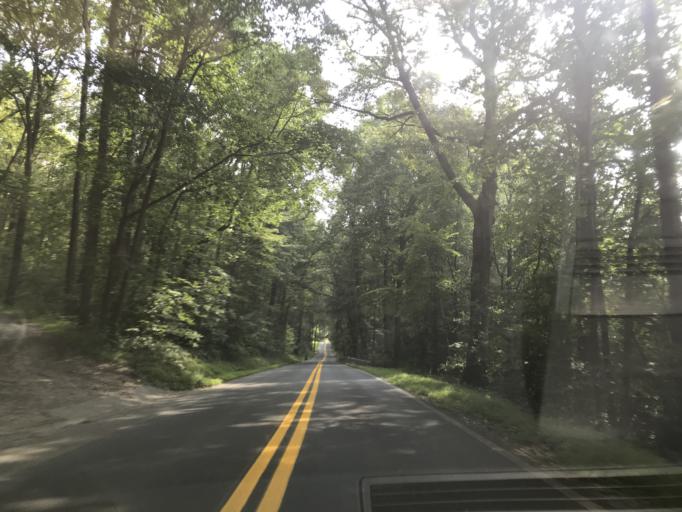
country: US
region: Maryland
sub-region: Carroll County
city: Manchester
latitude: 39.6704
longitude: -76.9004
